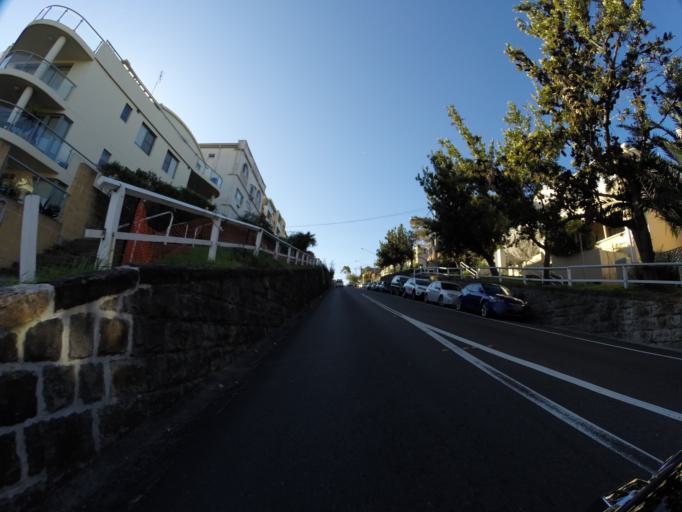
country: AU
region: New South Wales
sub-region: Randwick
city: Coogee
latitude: -33.9181
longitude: 151.2573
